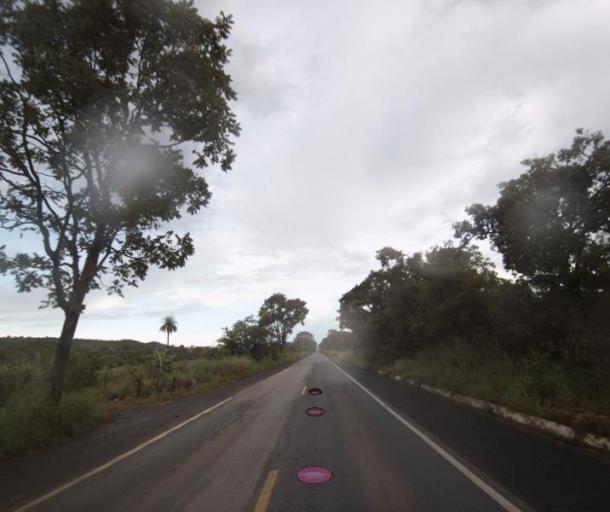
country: BR
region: Goias
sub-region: Porangatu
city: Porangatu
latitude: -13.9150
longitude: -49.0664
